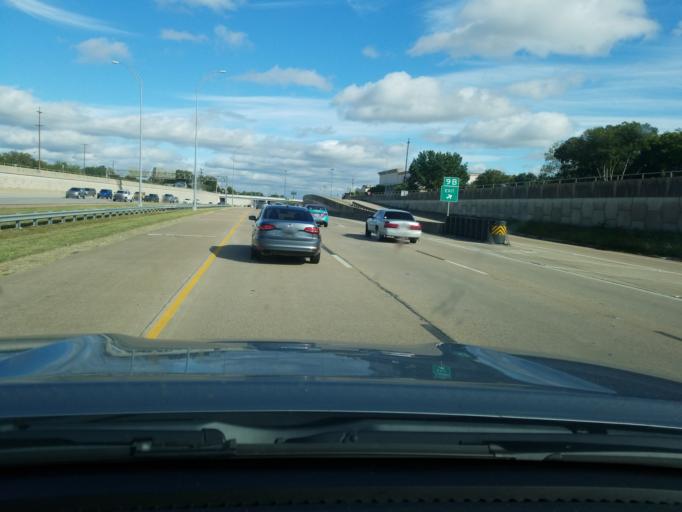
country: US
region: Texas
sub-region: Tarrant County
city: Westworth
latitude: 32.7344
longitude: -97.4115
